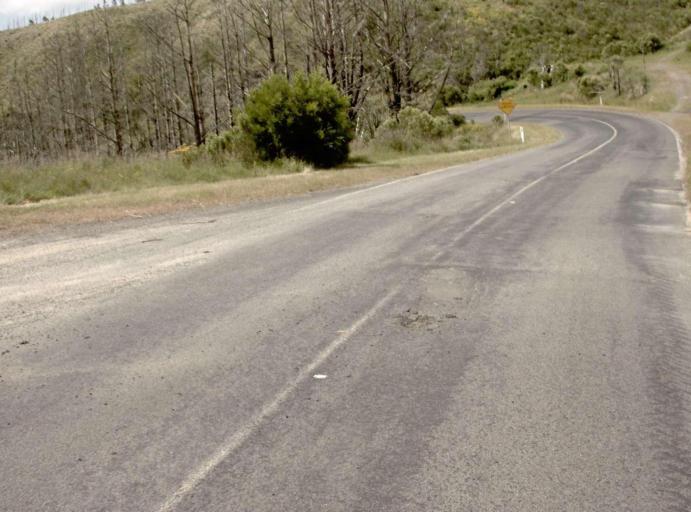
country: AU
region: Victoria
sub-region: Latrobe
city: Traralgon
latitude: -38.3922
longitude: 146.5555
